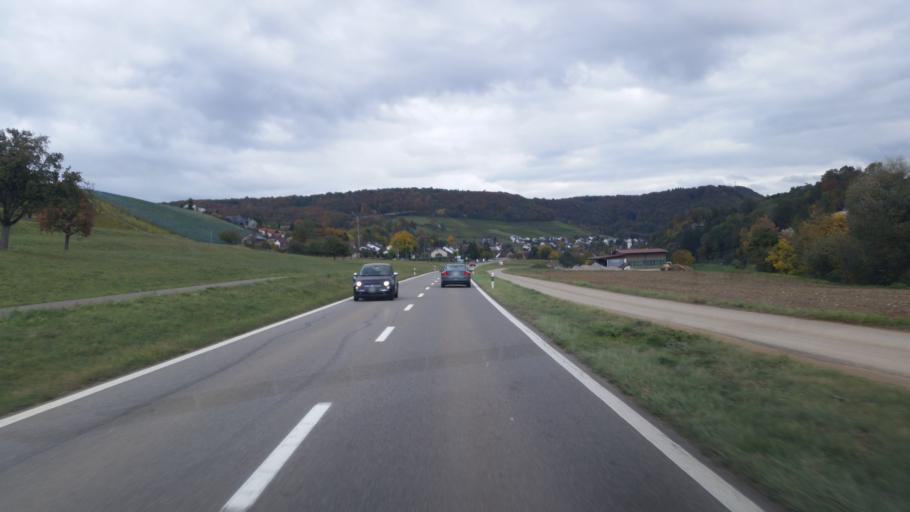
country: CH
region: Aargau
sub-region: Bezirk Zurzach
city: Tegerfelden
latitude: 47.5643
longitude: 8.2750
